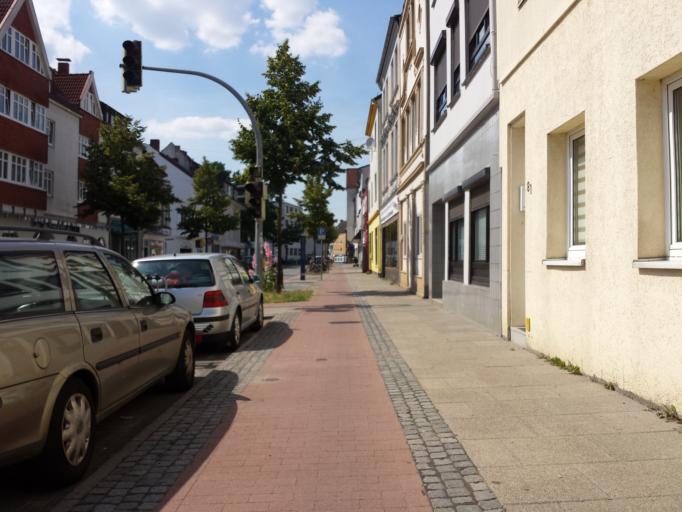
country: DE
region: Bremen
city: Bremen
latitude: 53.0807
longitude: 8.7742
